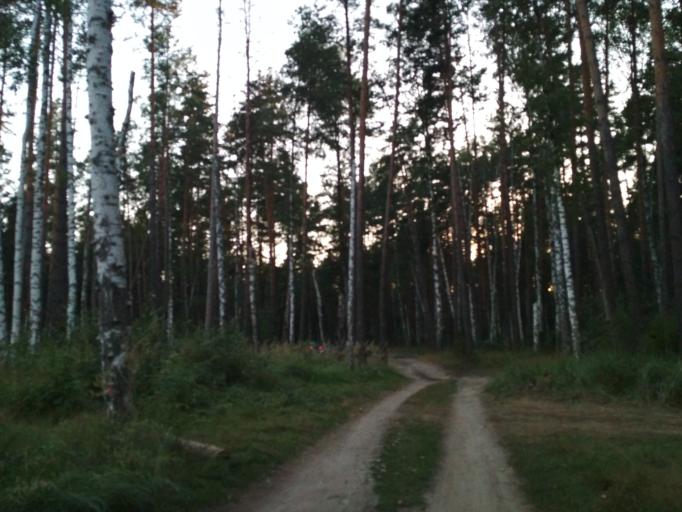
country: RU
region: Rjazan
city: Solotcha
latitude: 54.8260
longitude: 39.9501
